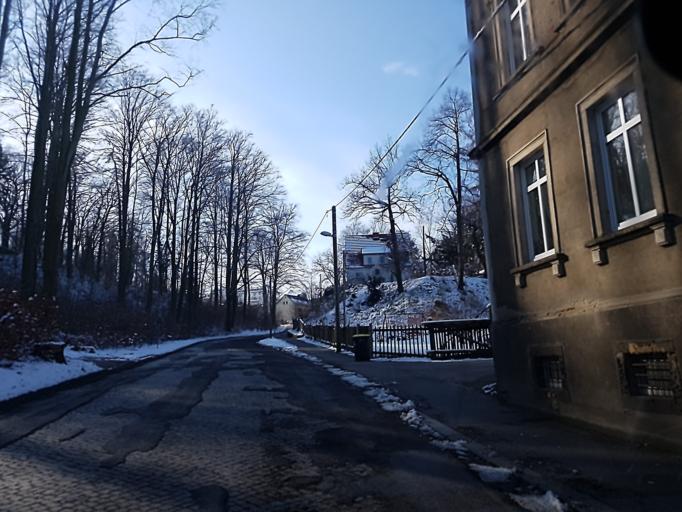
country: DE
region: Saxony
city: Leisnig
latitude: 51.1580
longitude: 12.9342
